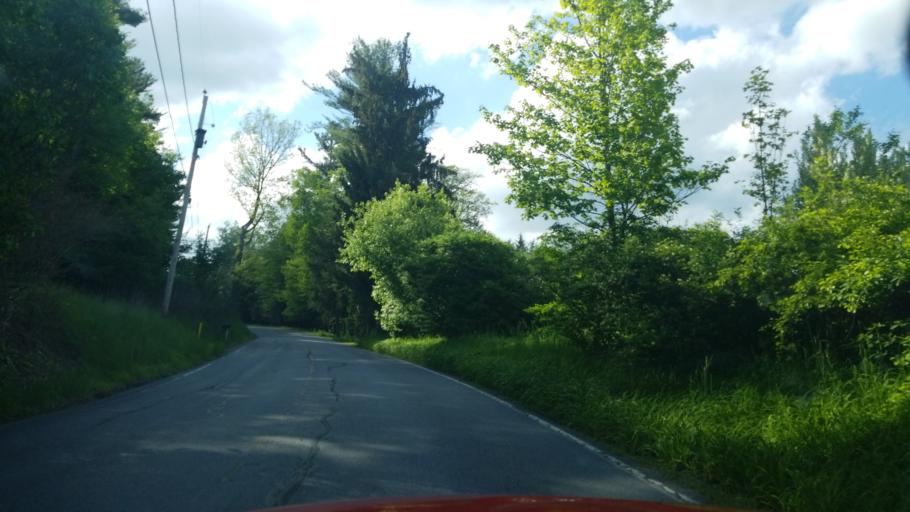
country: US
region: Pennsylvania
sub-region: Clearfield County
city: Hyde
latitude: 40.9734
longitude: -78.4419
